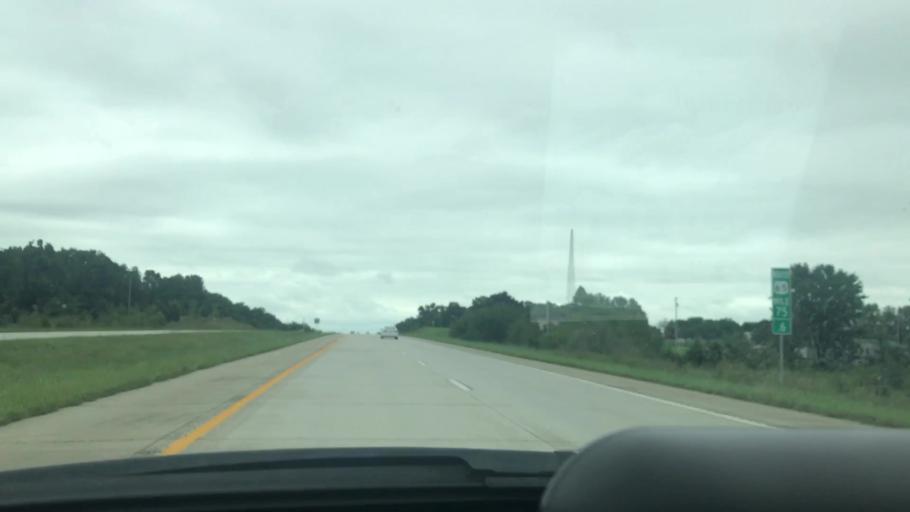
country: US
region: Missouri
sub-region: Dallas County
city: Buffalo
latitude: 37.5380
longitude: -93.1374
